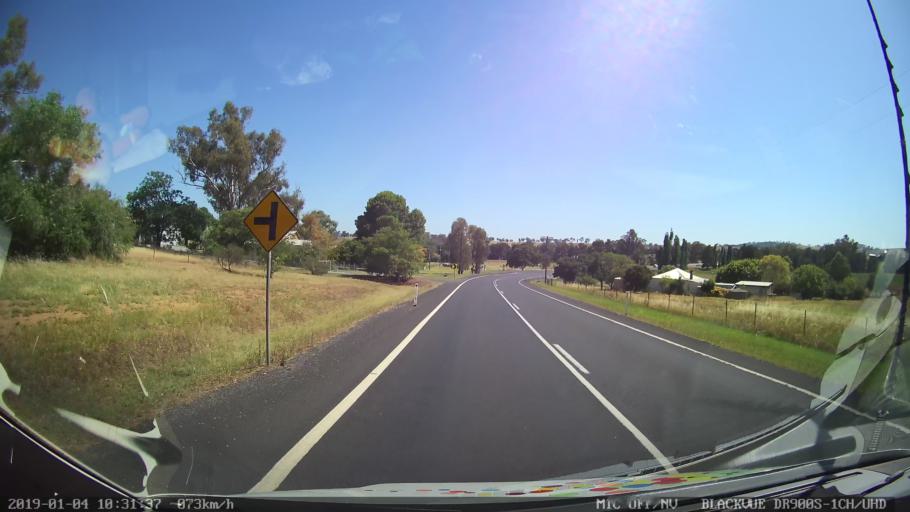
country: AU
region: New South Wales
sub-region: Cabonne
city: Canowindra
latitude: -33.3327
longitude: 148.6326
